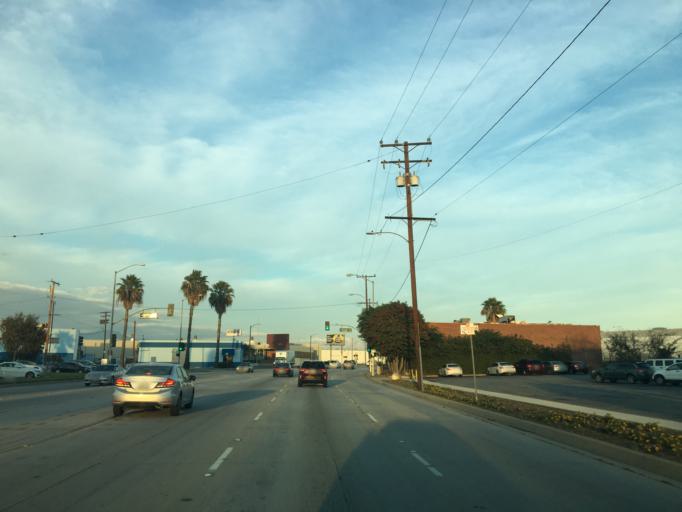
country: US
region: California
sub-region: Los Angeles County
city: Commerce
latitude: 33.9993
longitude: -118.1369
